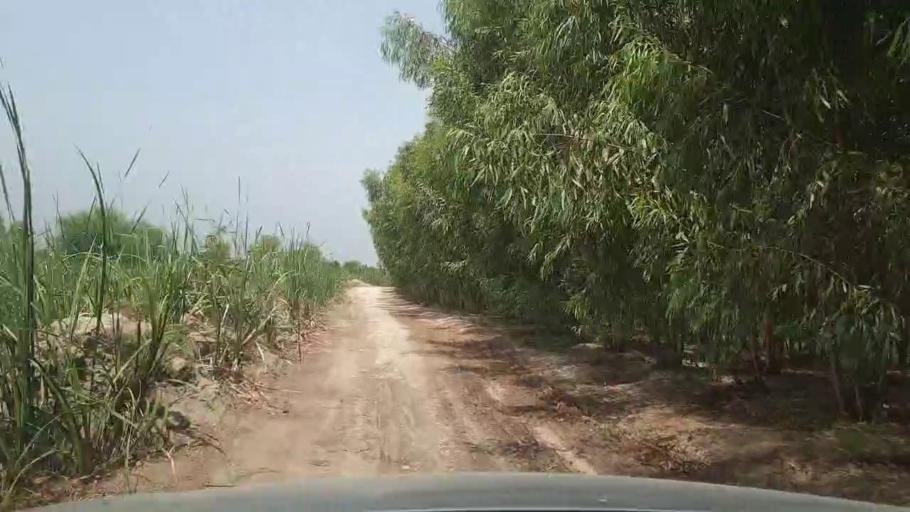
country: PK
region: Sindh
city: Garhi Yasin
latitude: 27.9456
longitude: 68.4295
